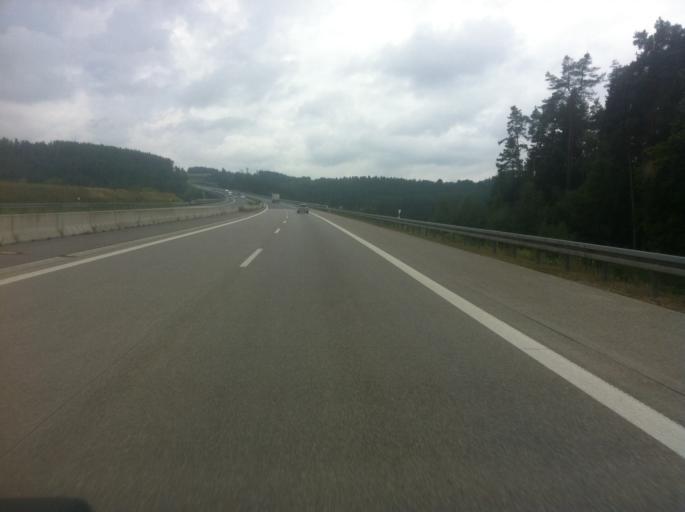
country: DE
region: Bavaria
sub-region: Upper Palatinate
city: Pfreimd
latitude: 49.4864
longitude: 12.1383
